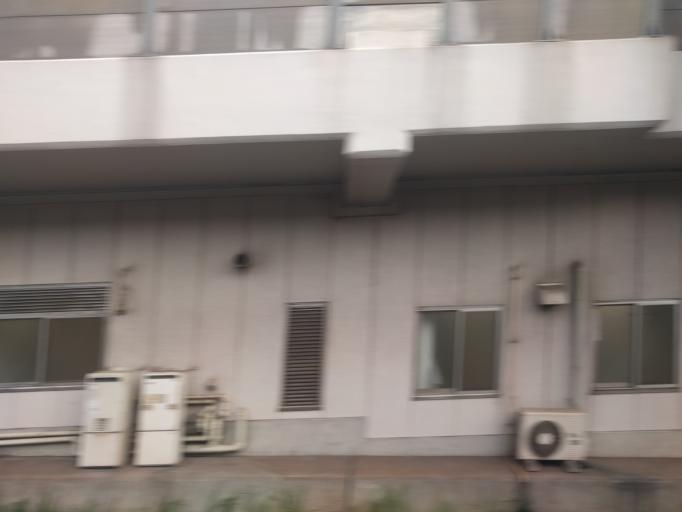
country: JP
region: Tokyo
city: Chofugaoka
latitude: 35.5829
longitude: 139.5766
